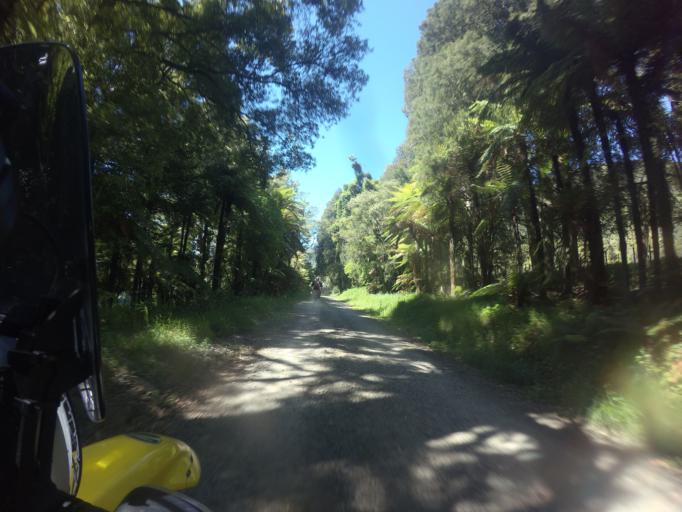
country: NZ
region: Bay of Plenty
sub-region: Opotiki District
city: Opotiki
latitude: -38.2984
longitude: 177.3345
